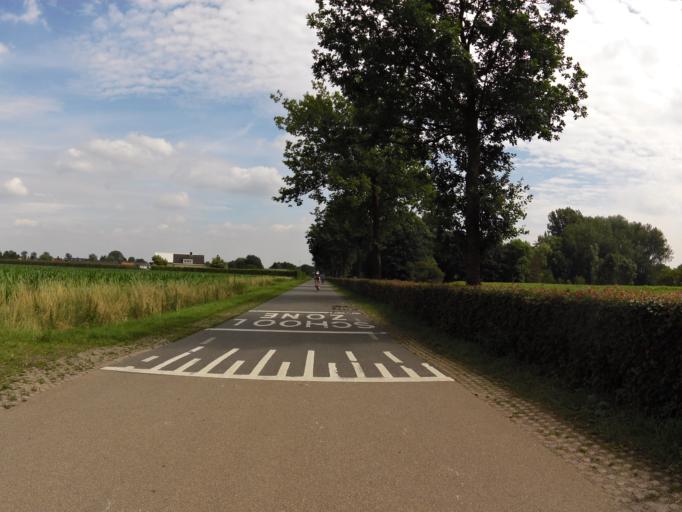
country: NL
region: South Holland
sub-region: Gemeente Leerdam
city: Leerdam
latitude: 51.8827
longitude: 5.1441
